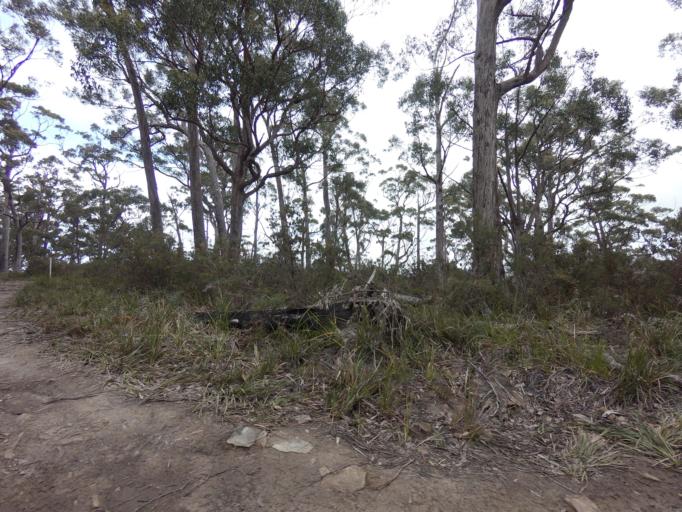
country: AU
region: Tasmania
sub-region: Huon Valley
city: Geeveston
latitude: -43.4763
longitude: 146.9340
